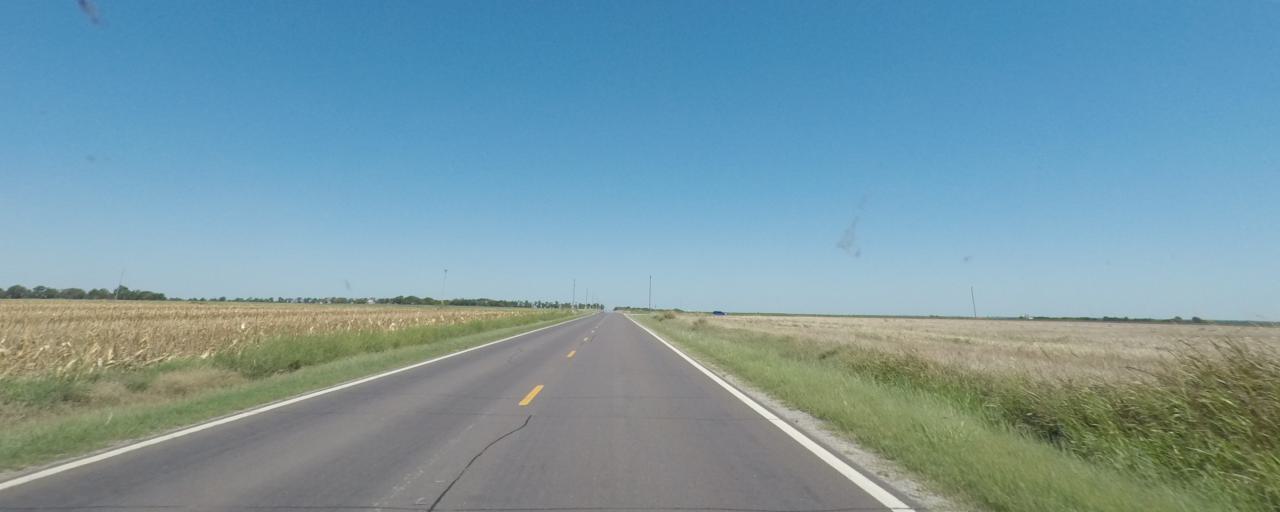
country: US
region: Kansas
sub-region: Sumner County
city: Wellington
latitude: 37.2005
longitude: -97.4022
